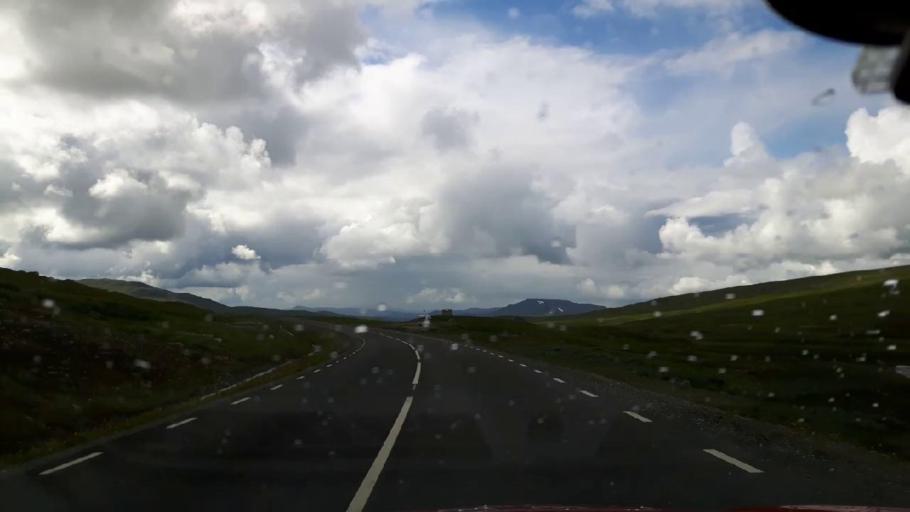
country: NO
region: Nordland
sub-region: Hattfjelldal
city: Hattfjelldal
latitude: 65.0475
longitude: 14.3347
